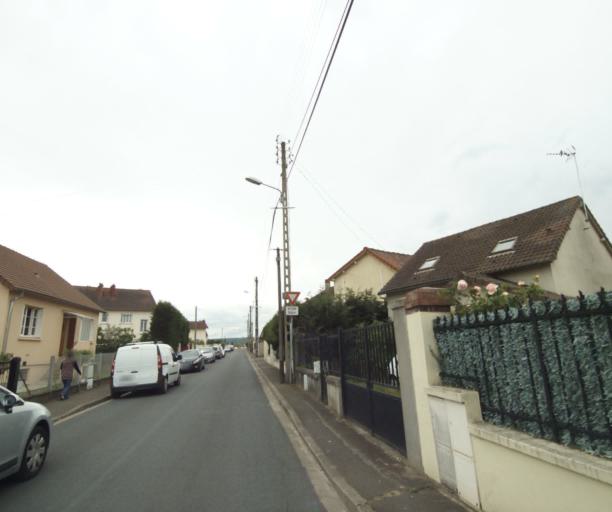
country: FR
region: Ile-de-France
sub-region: Departement des Yvelines
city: Les Mureaux
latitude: 48.9871
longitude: 1.9031
